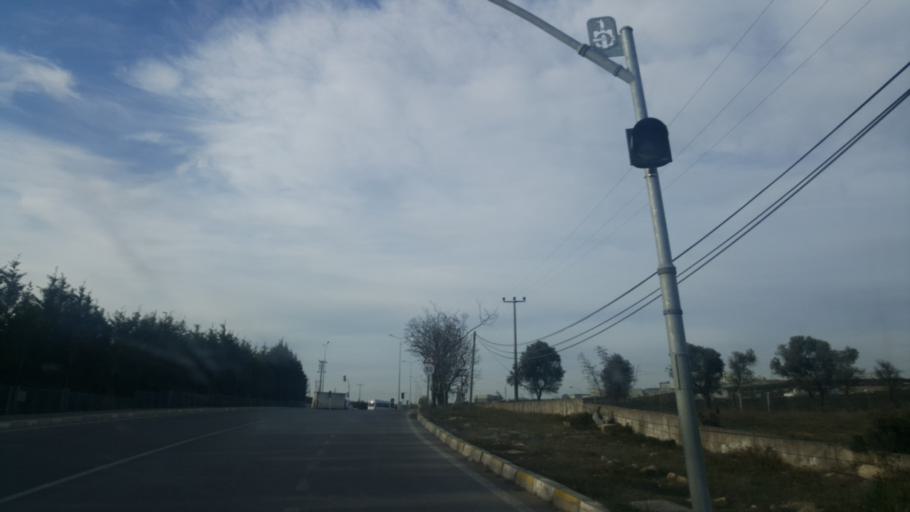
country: TR
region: Kocaeli
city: Tavsancil
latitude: 40.7996
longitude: 29.5524
